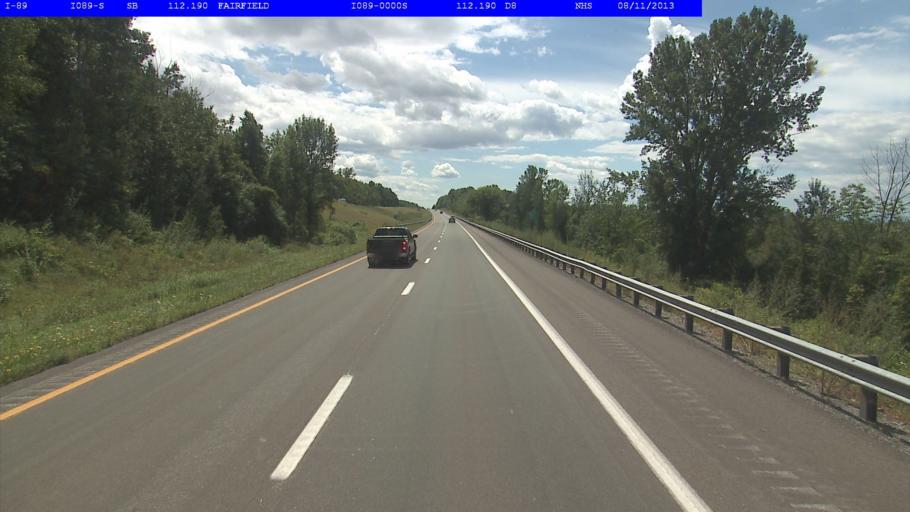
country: US
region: Vermont
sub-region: Franklin County
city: Saint Albans
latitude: 44.7728
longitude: -73.0754
